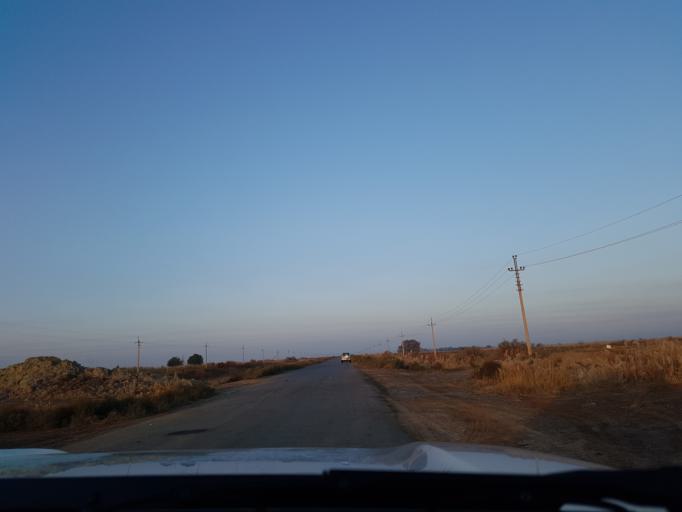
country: TM
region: Dasoguz
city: Koeneuergench
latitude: 41.8438
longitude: 58.7044
